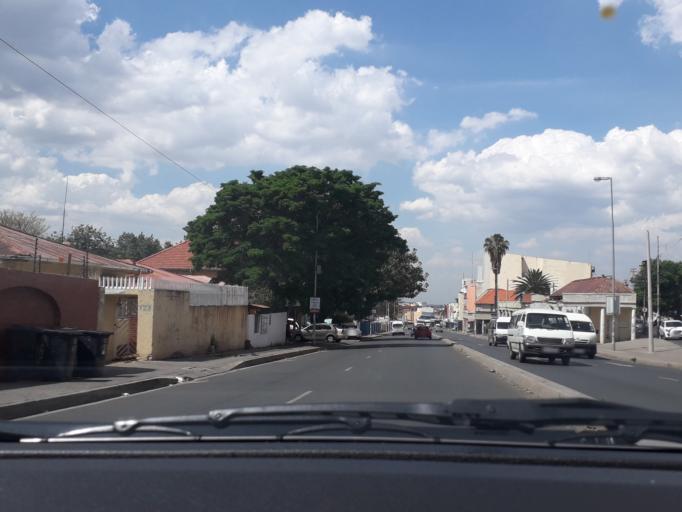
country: ZA
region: Gauteng
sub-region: City of Johannesburg Metropolitan Municipality
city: Johannesburg
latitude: -26.1677
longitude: 28.0777
